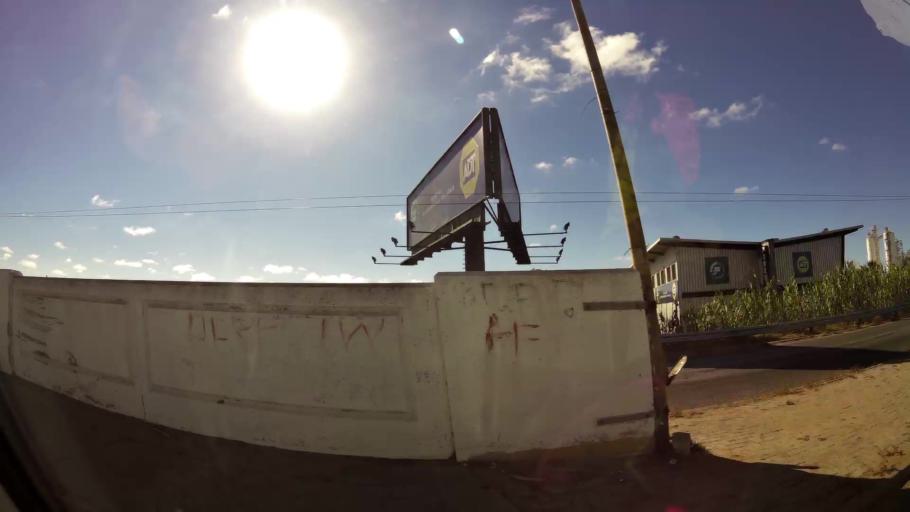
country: ZA
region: Limpopo
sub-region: Capricorn District Municipality
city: Polokwane
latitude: -23.8892
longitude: 29.4462
